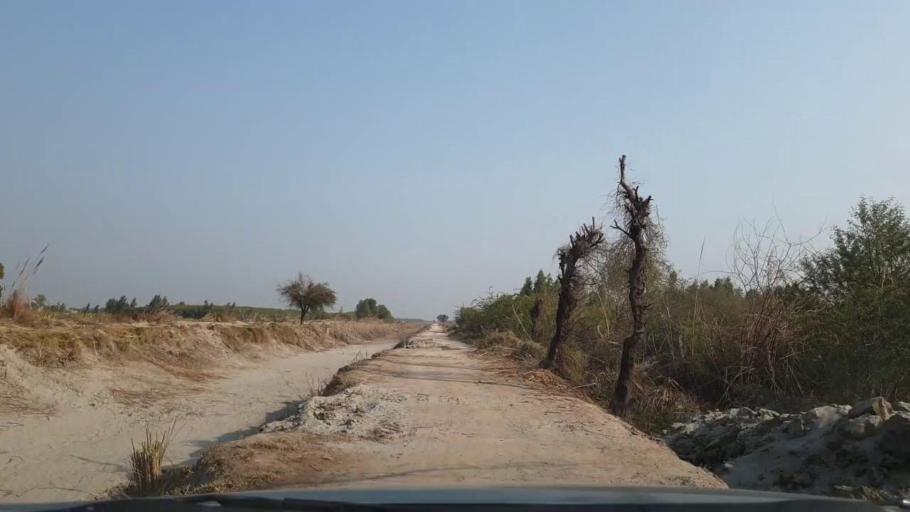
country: PK
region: Sindh
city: Tando Adam
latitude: 25.6474
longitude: 68.5974
